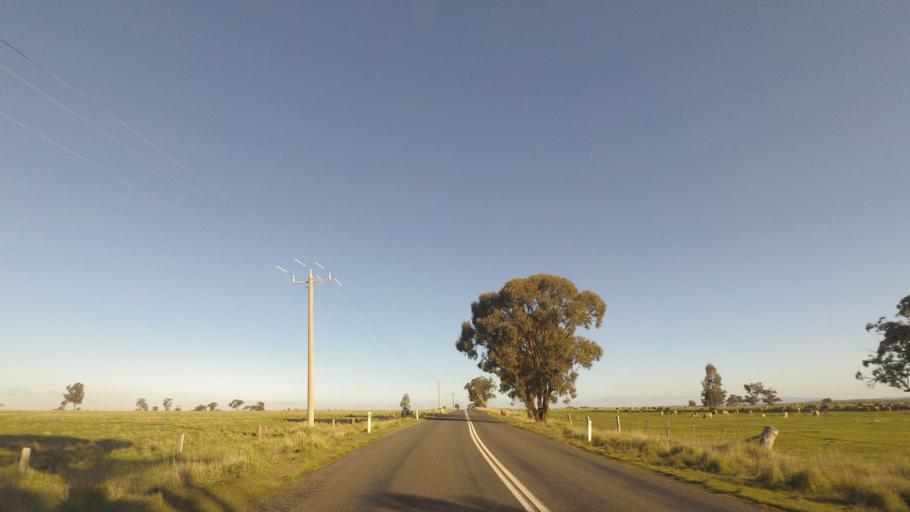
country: AU
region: Victoria
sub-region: Greater Bendigo
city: Kennington
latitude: -36.8211
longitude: 144.5164
